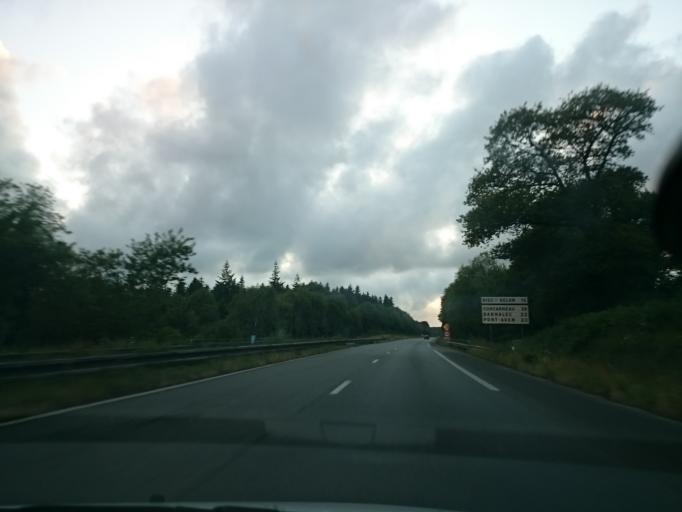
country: FR
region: Brittany
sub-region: Departement du Finistere
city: Quimperle
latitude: 47.8512
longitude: -3.5163
